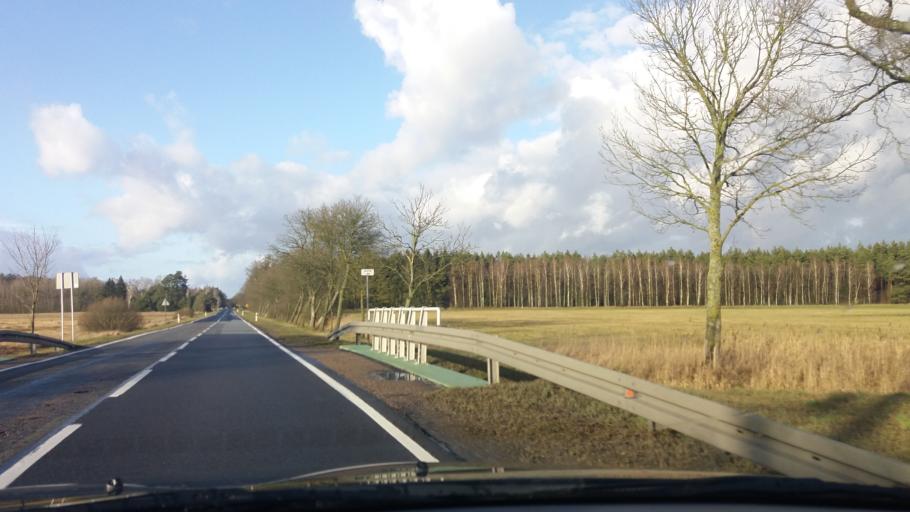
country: PL
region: Masovian Voivodeship
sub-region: Powiat przasnyski
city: Chorzele
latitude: 53.3230
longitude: 20.9057
